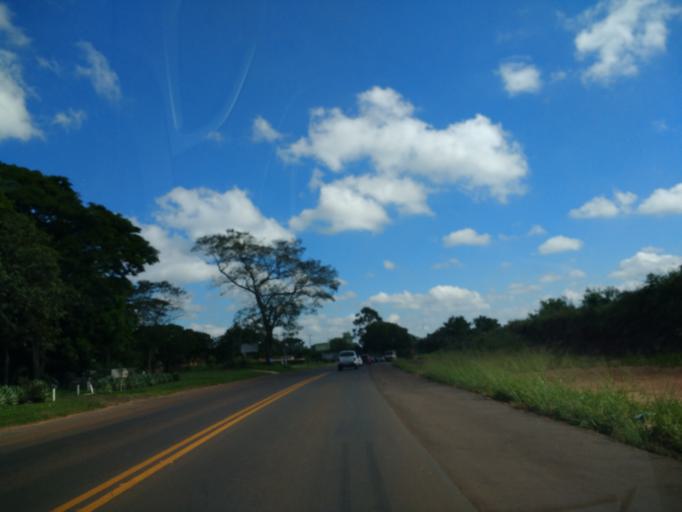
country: BR
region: Parana
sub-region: Umuarama
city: Umuarama
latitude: -23.8245
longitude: -53.3393
